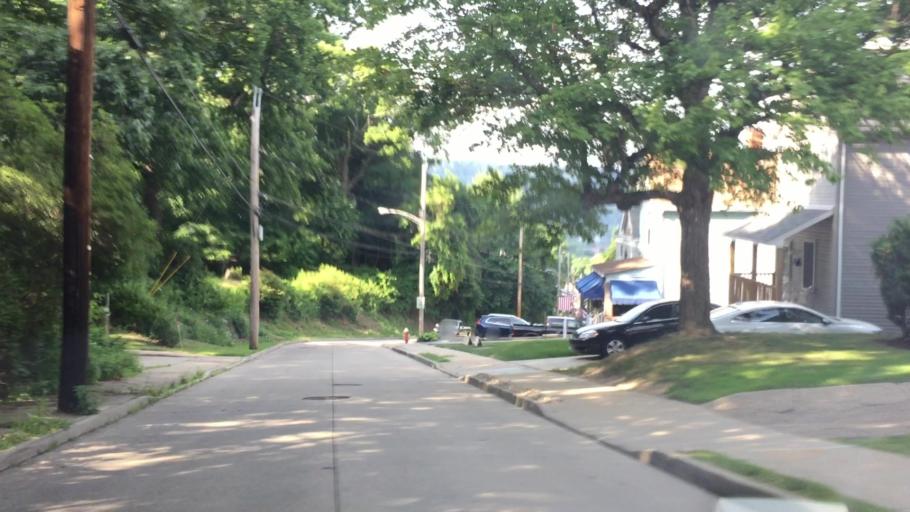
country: US
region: Pennsylvania
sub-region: Allegheny County
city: Coraopolis
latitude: 40.5130
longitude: -80.1717
